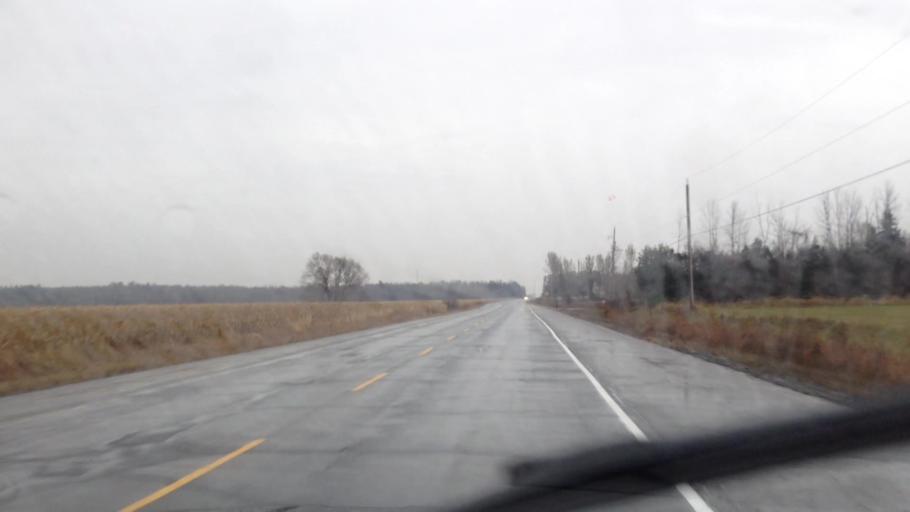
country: CA
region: Ontario
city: Clarence-Rockland
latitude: 45.4432
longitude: -75.4198
